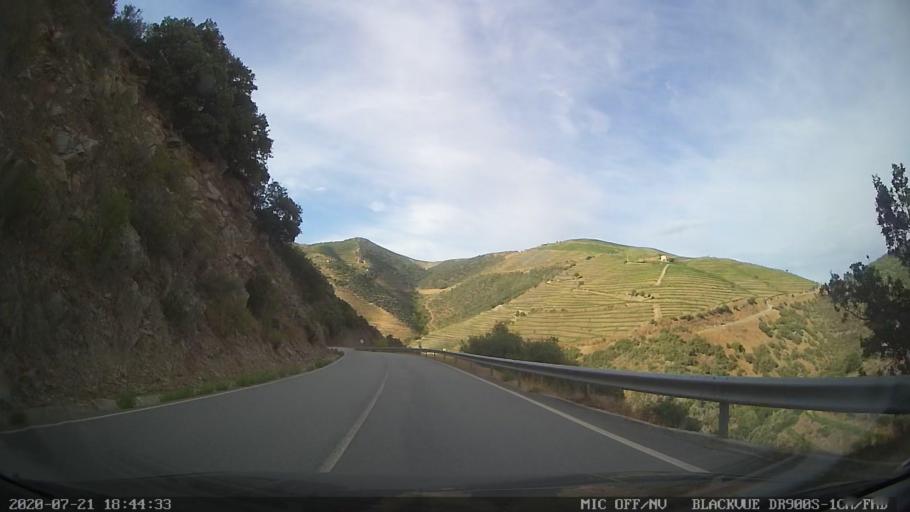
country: PT
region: Viseu
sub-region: Sao Joao da Pesqueira
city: Sao Joao da Pesqueira
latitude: 41.1188
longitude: -7.4531
